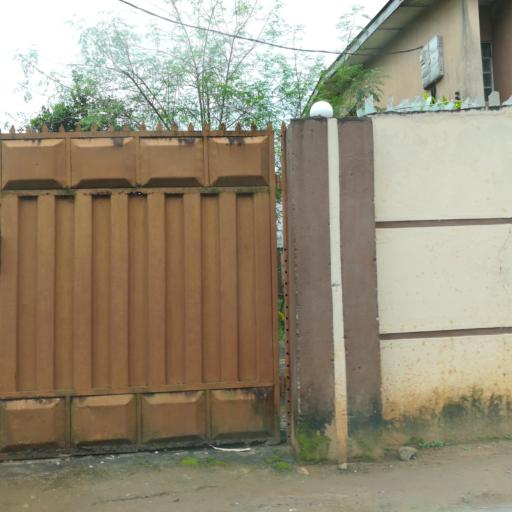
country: NG
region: Lagos
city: Agege
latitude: 6.6032
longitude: 3.2954
